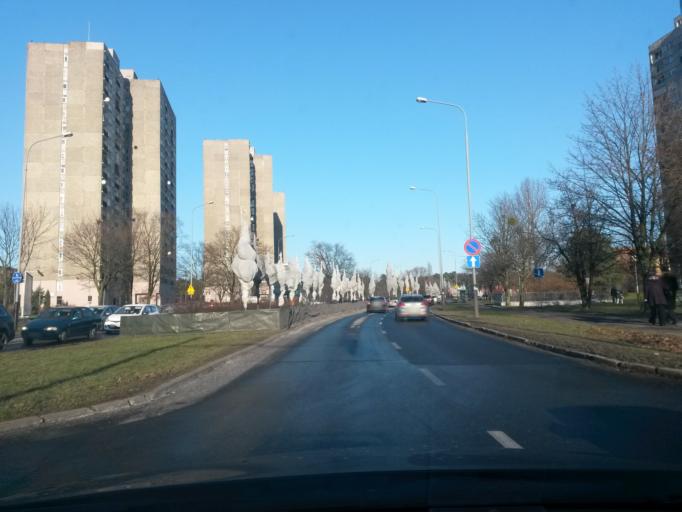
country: PL
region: Greater Poland Voivodeship
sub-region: Poznan
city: Poznan
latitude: 52.3923
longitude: 16.9804
